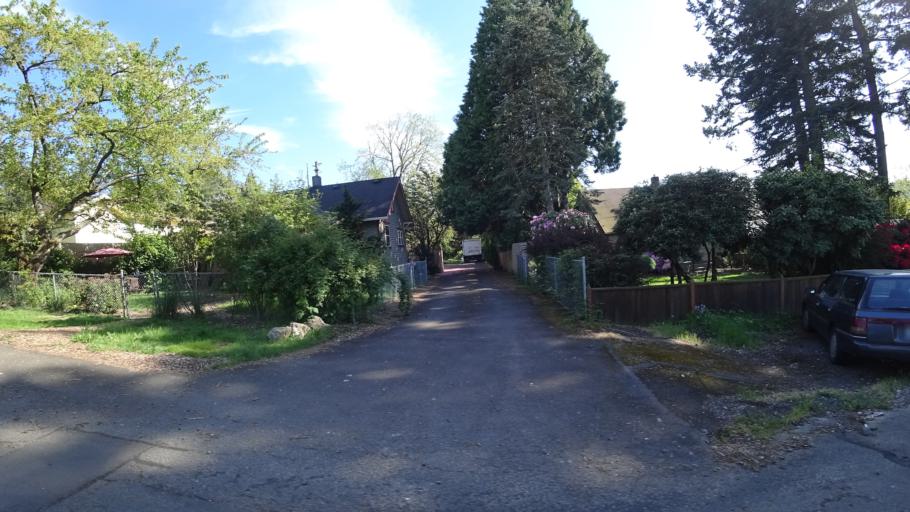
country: US
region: Oregon
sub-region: Clackamas County
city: Milwaukie
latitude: 45.4546
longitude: -122.6340
